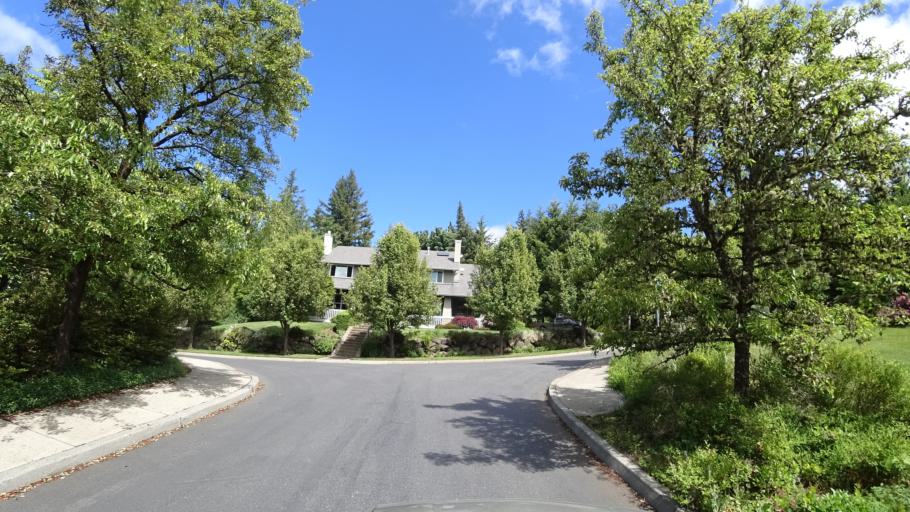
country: US
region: Oregon
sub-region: Washington County
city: Bethany
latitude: 45.5985
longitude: -122.8256
